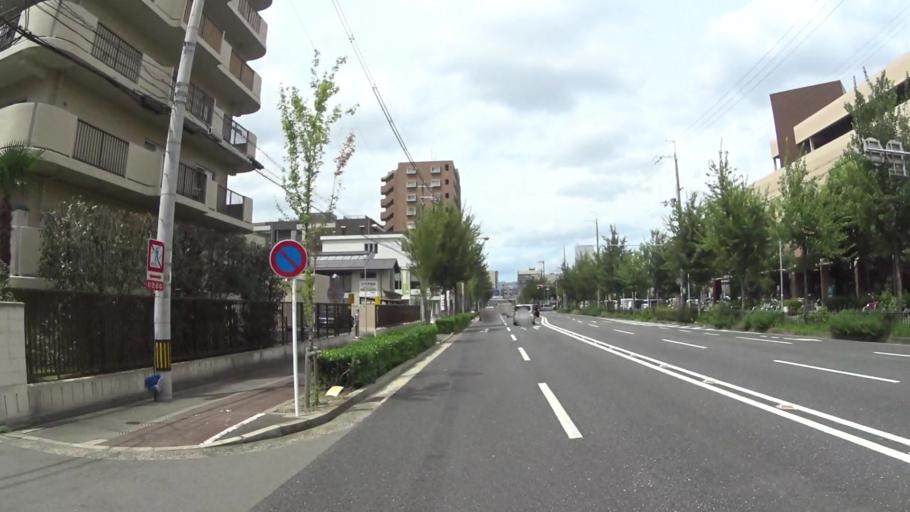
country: JP
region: Kyoto
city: Muko
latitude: 34.9748
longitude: 135.7353
